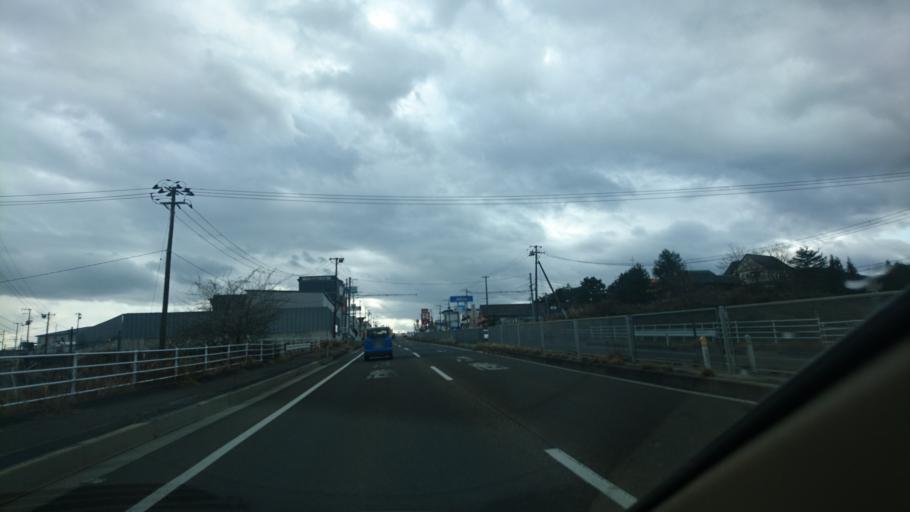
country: JP
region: Miyagi
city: Tomiya
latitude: 38.4103
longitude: 140.8868
